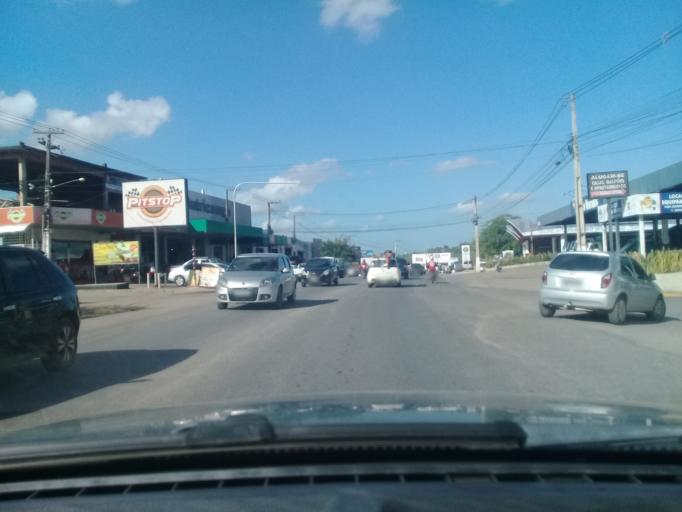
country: BR
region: Pernambuco
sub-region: Vitoria De Santo Antao
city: Vitoria de Santo Antao
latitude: -8.1129
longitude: -35.2932
